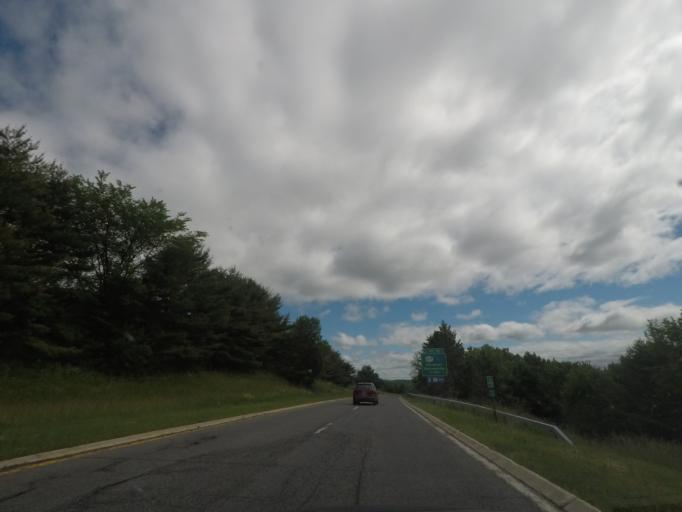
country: US
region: New York
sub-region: Columbia County
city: Philmont
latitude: 42.2609
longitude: -73.6138
